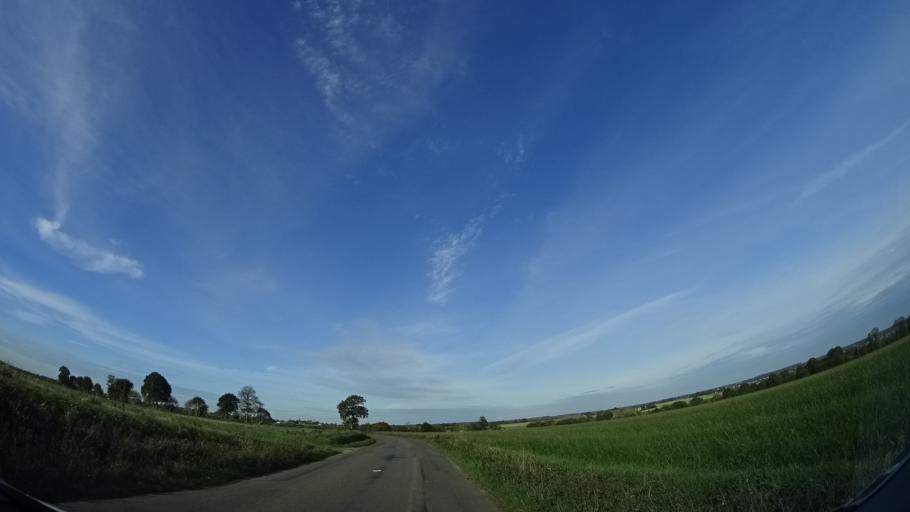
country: FR
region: Brittany
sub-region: Departement d'Ille-et-Vilaine
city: Geveze
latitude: 48.2101
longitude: -1.8270
